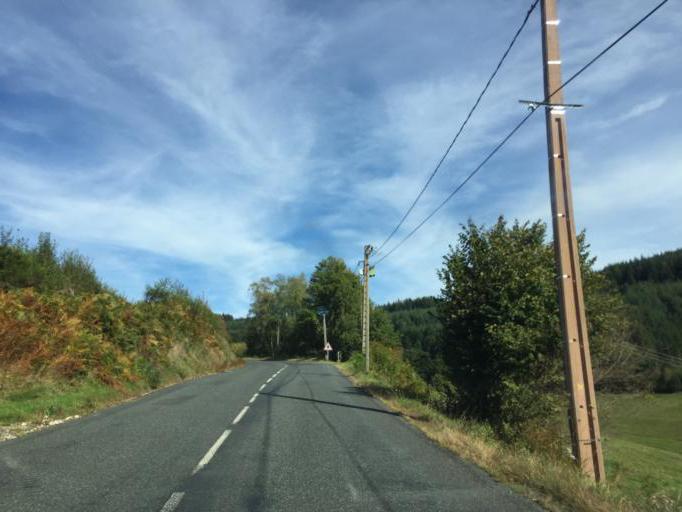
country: FR
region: Rhone-Alpes
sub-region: Departement de la Loire
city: Belmont-de-la-Loire
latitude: 46.1306
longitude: 4.4014
